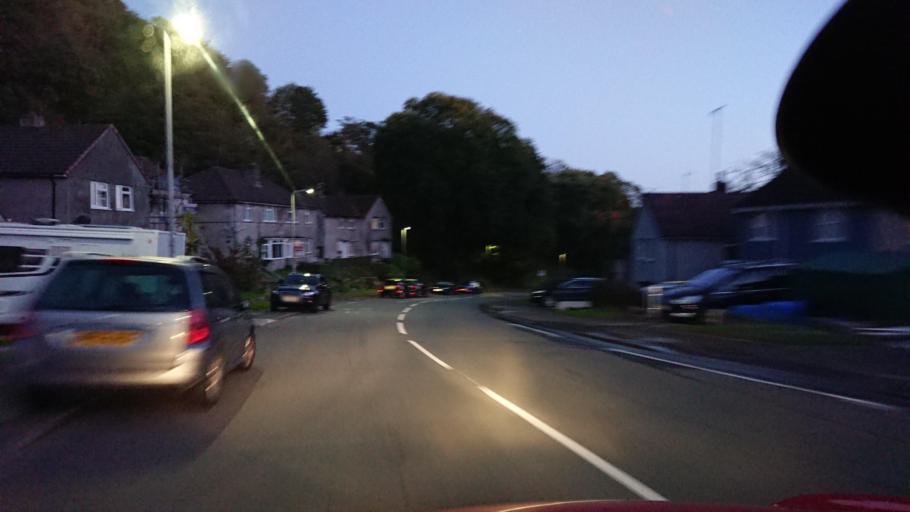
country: GB
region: England
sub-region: Plymouth
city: Plymstock
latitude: 50.3872
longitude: -4.1030
